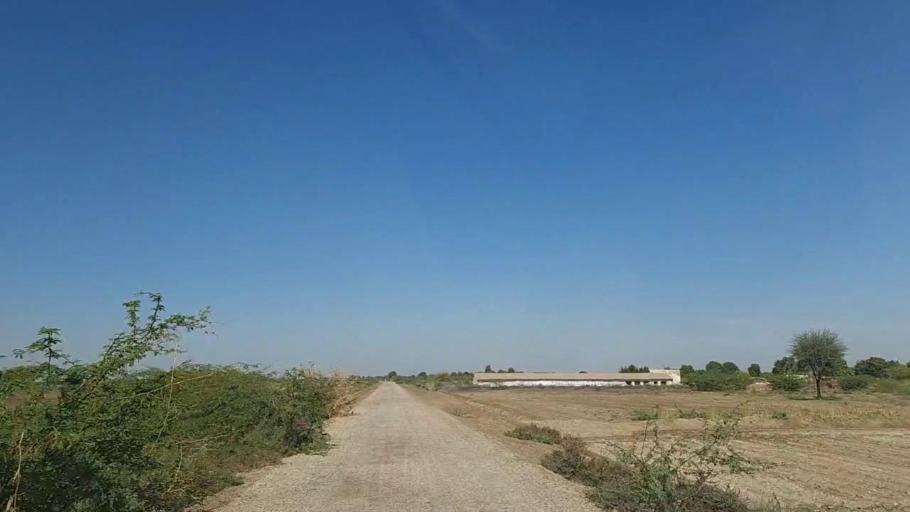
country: PK
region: Sindh
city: Samaro
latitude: 25.3051
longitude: 69.5148
